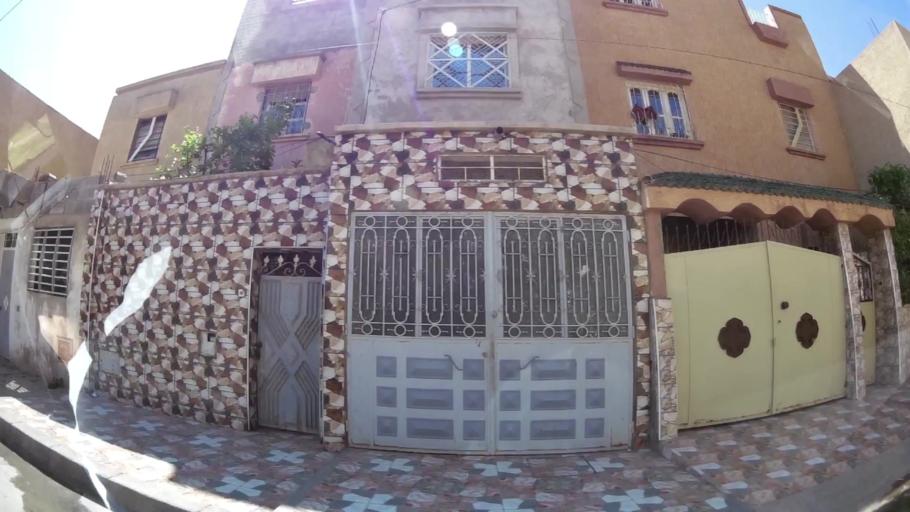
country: MA
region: Oriental
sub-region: Oujda-Angad
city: Oujda
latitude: 34.6734
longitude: -1.9437
